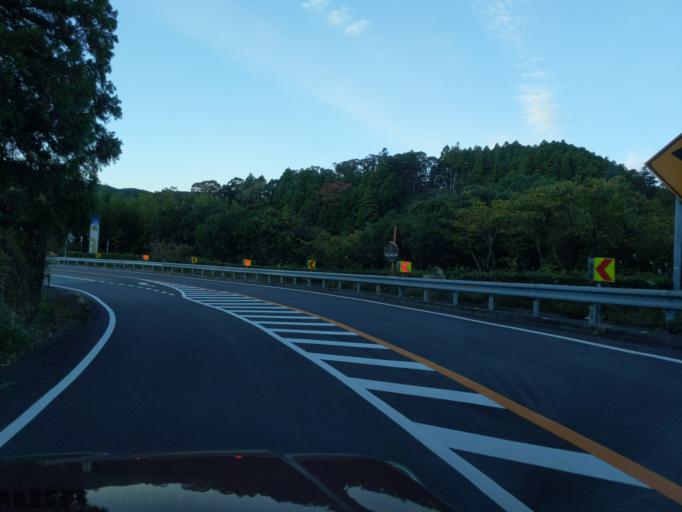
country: JP
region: Tokushima
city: Anan
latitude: 33.6988
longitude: 134.4352
